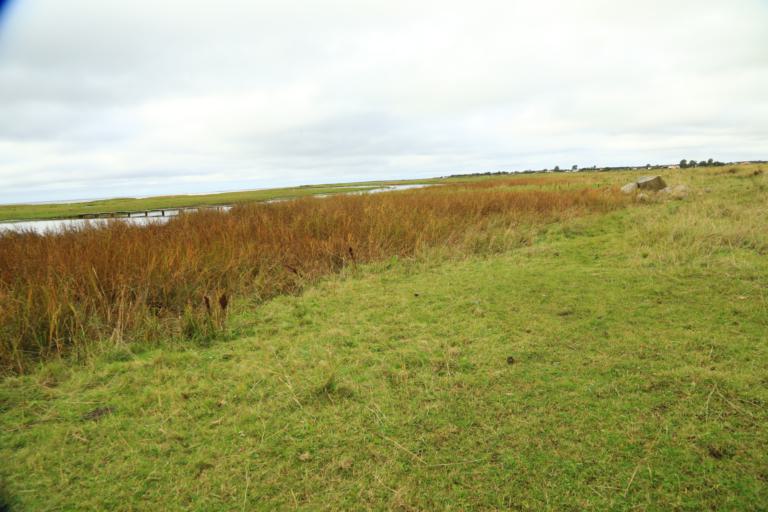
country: SE
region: Halland
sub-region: Varbergs Kommun
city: Tvaaker
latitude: 57.0186
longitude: 12.3390
